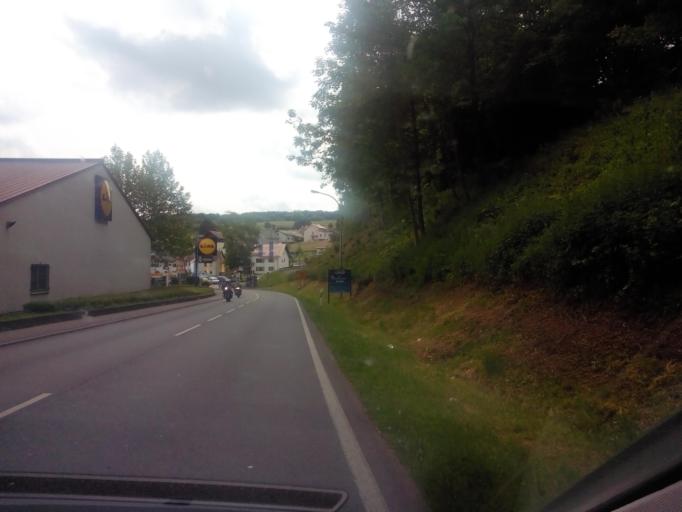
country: DE
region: Saarland
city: Eppelborn
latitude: 49.4071
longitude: 6.9535
